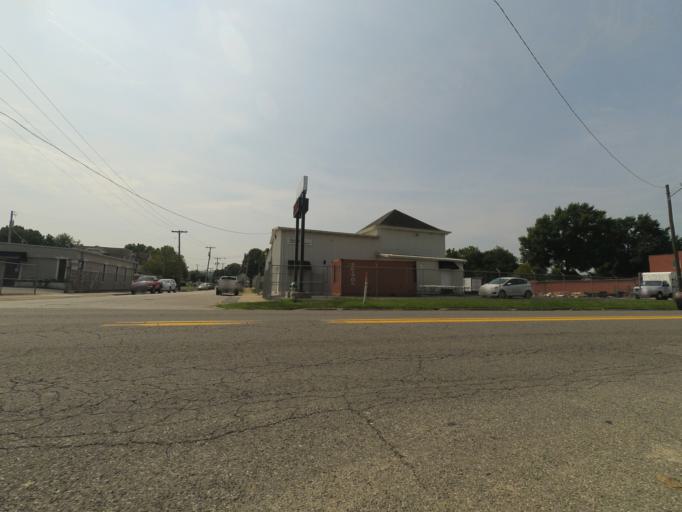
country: US
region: West Virginia
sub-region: Cabell County
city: Huntington
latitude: 38.4166
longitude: -82.4338
